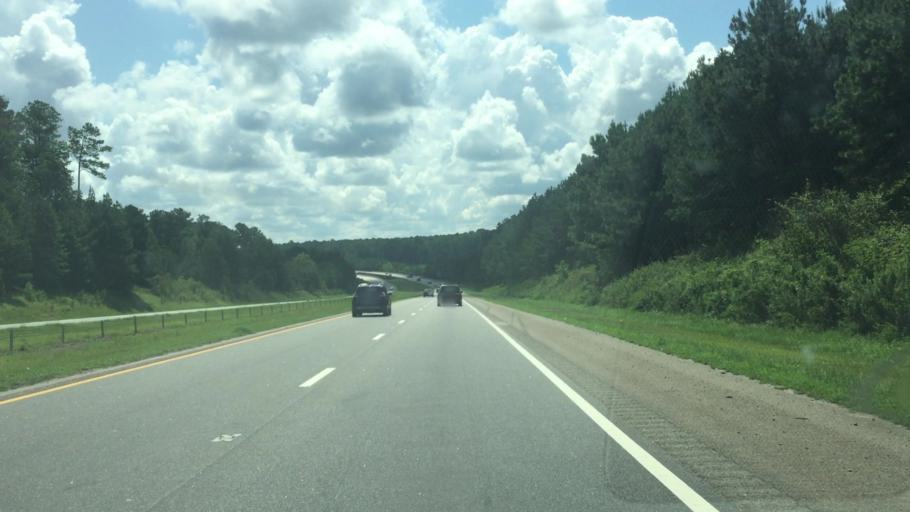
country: US
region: North Carolina
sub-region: Richmond County
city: Cordova
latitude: 34.9254
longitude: -79.8192
